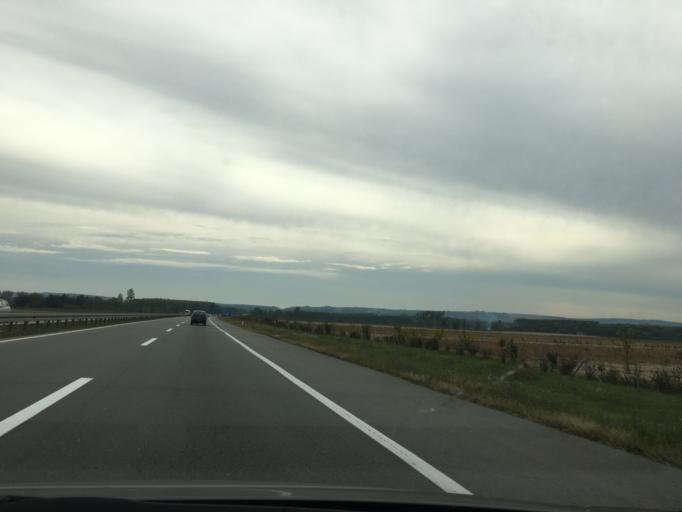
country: RS
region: Autonomna Pokrajina Vojvodina
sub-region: Juznobacki Okrug
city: Kovilj
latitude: 45.2009
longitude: 20.0725
